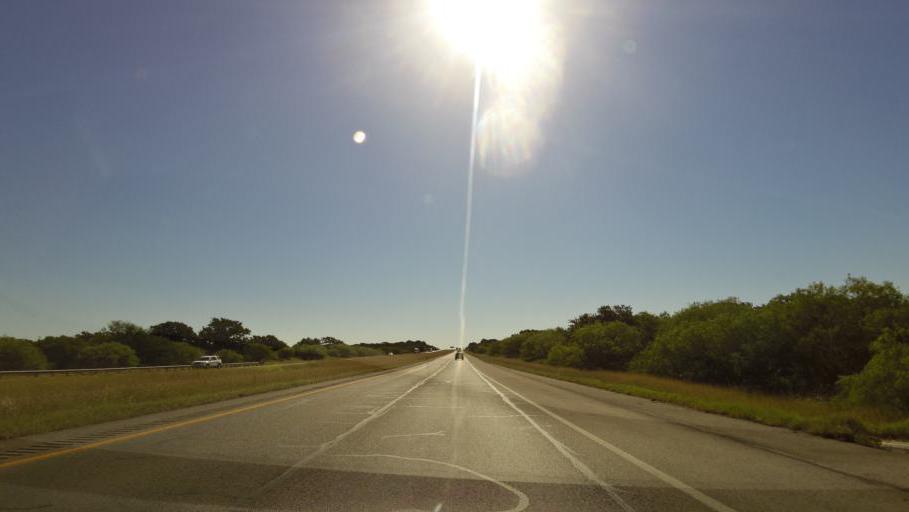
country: US
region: Texas
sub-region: Guadalupe County
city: Seguin
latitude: 29.6148
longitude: -97.8257
